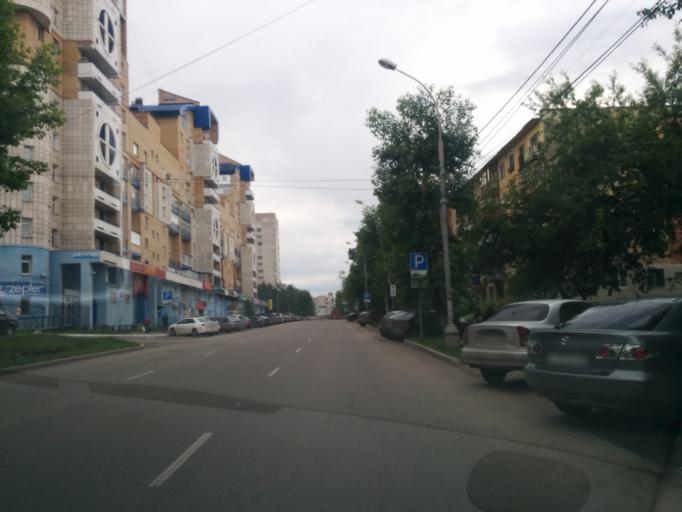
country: RU
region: Perm
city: Perm
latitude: 58.0042
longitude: 56.2137
